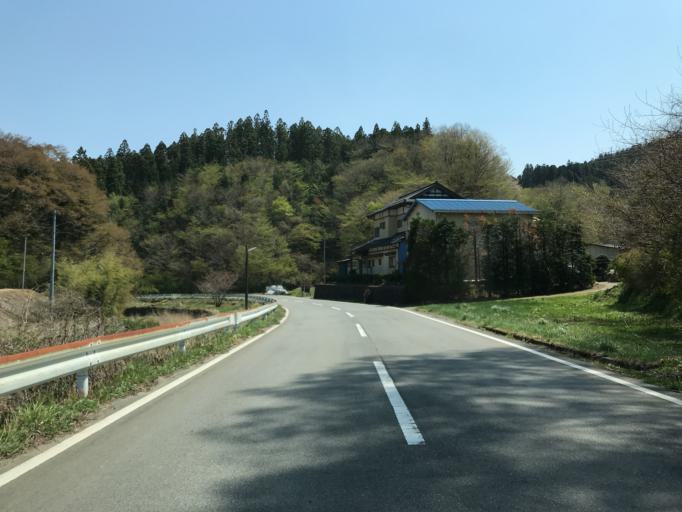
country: JP
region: Ibaraki
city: Kitaibaraki
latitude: 36.9675
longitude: 140.6547
